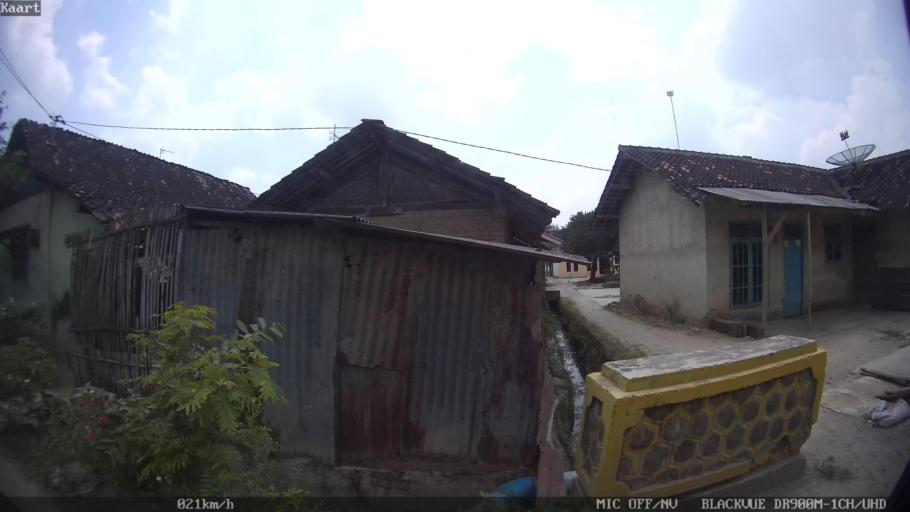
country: ID
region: Lampung
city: Pringsewu
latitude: -5.3494
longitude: 104.9904
